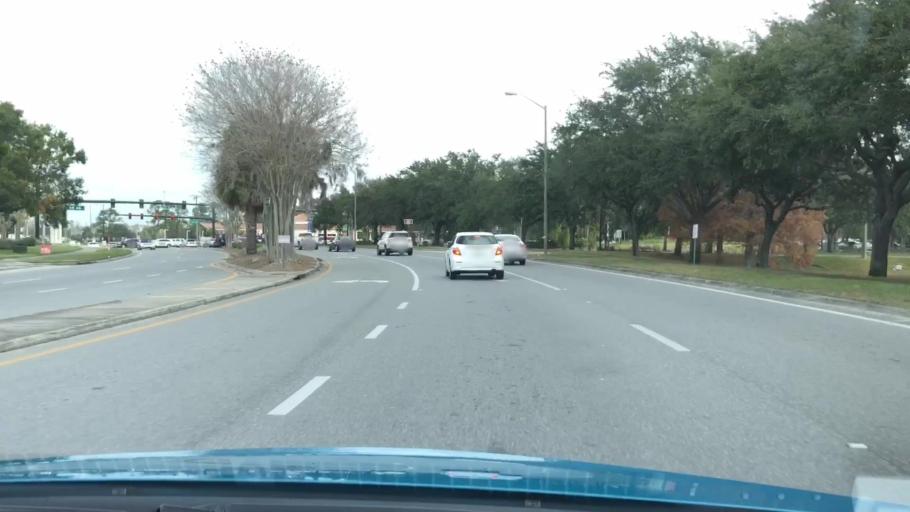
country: US
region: Florida
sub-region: Seminole County
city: Lake Mary
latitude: 28.8100
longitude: -81.3345
